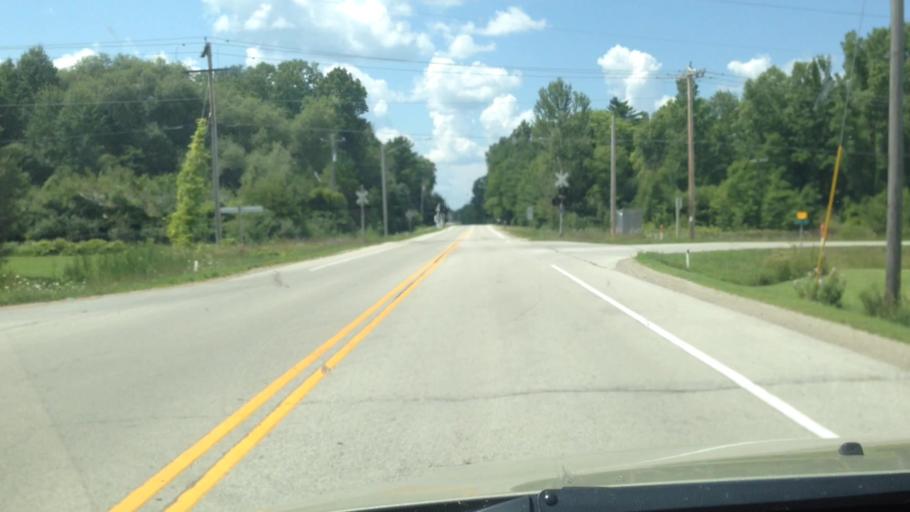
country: US
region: Wisconsin
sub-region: Brown County
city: Suamico
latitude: 44.6382
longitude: -88.0695
